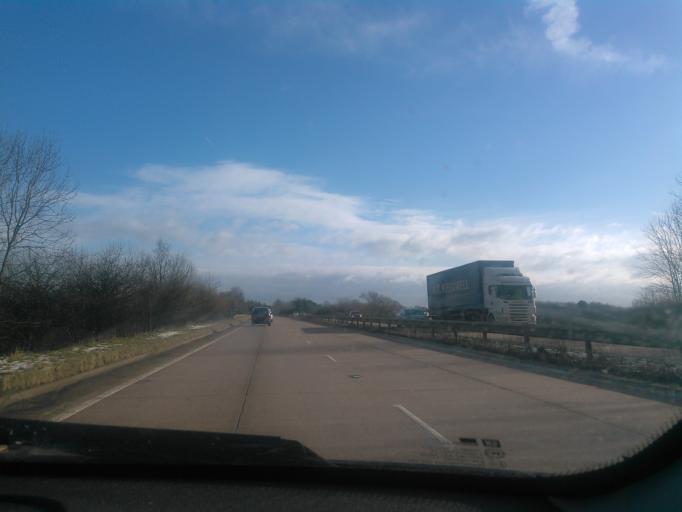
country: GB
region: England
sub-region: Staffordshire
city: Cheadle
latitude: 52.9365
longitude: -1.9813
